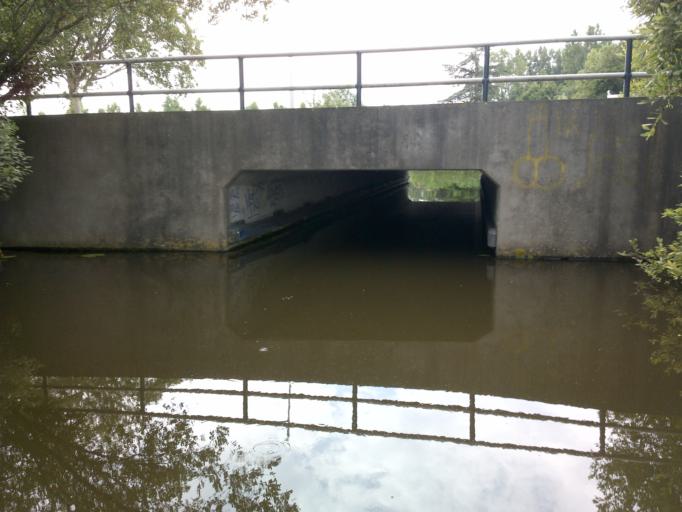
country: NL
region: South Holland
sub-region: Gemeente Teylingen
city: Sassenheim
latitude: 52.2225
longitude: 4.5393
